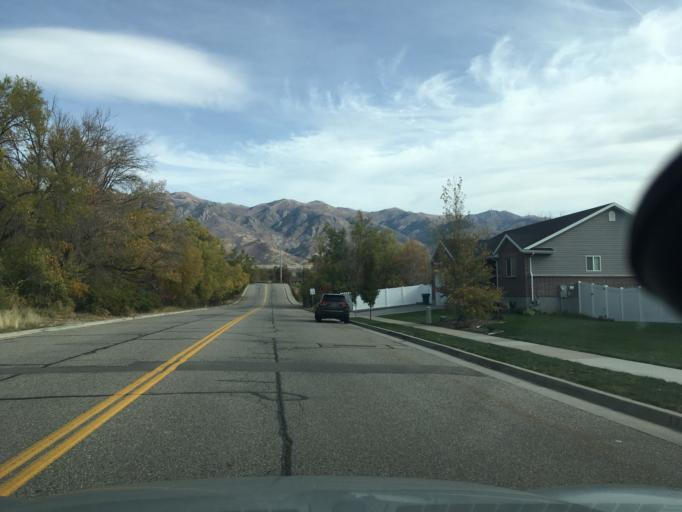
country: US
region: Utah
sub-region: Davis County
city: Layton
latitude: 41.0698
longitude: -111.9623
